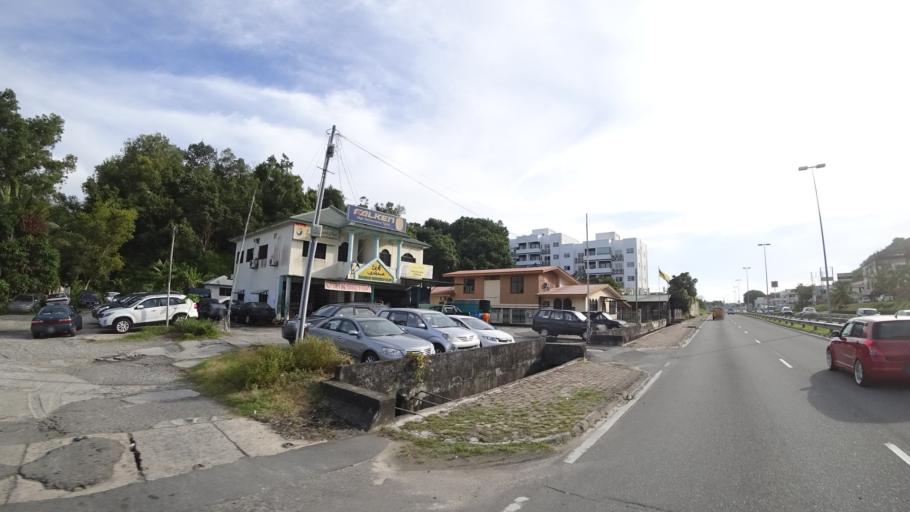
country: BN
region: Brunei and Muara
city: Bandar Seri Begawan
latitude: 4.8586
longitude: 114.8949
